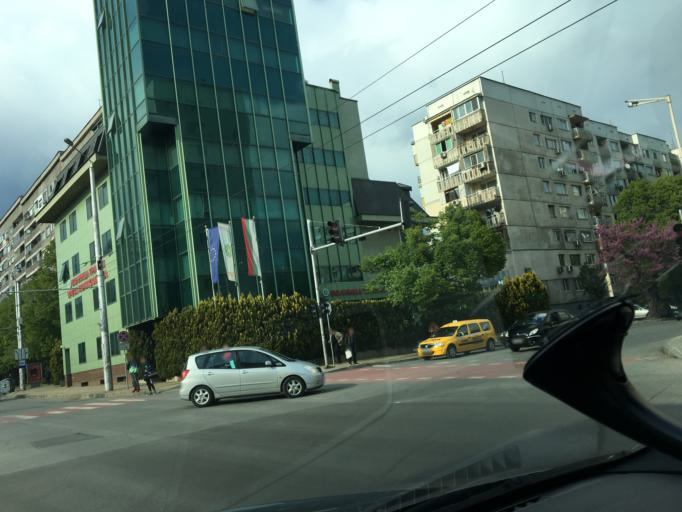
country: BG
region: Stara Zagora
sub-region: Obshtina Stara Zagora
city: Stara Zagora
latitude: 42.4231
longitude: 25.6354
